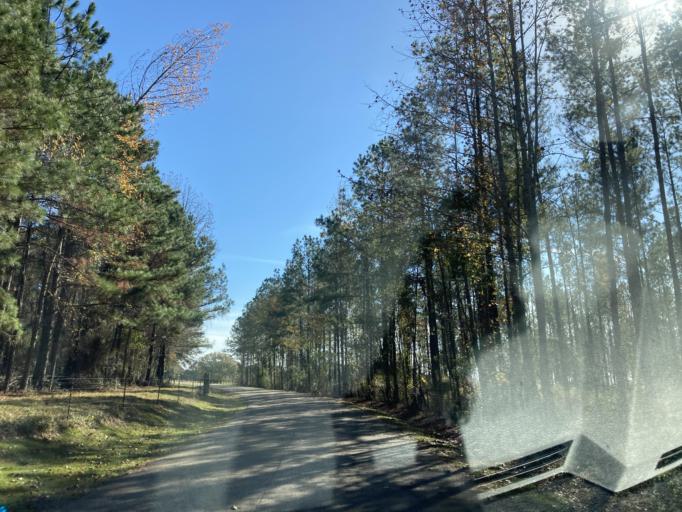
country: US
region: Mississippi
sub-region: Lamar County
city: Sumrall
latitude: 31.2626
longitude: -89.5262
